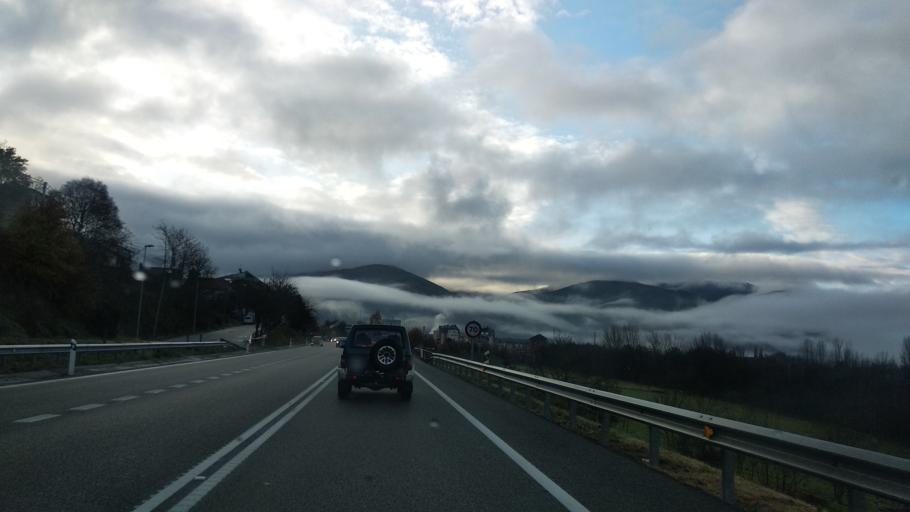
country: ES
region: Catalonia
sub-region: Provincia de Lleida
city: la Seu d'Urgell
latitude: 42.3620
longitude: 1.4548
